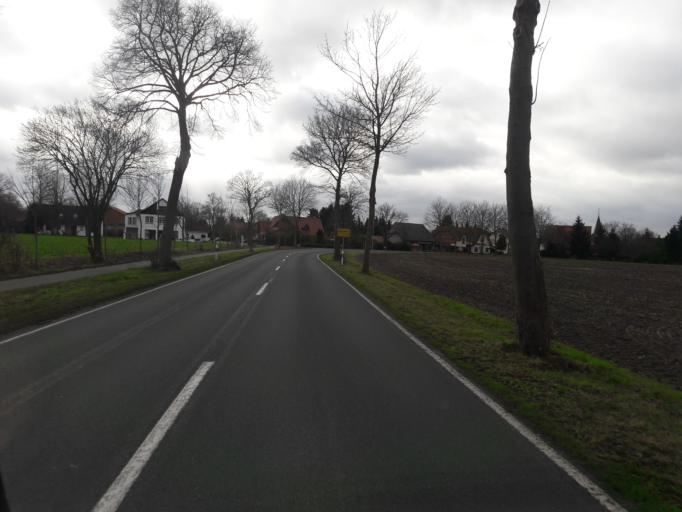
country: DE
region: Lower Saxony
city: Warmsen
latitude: 52.4588
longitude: 8.8523
